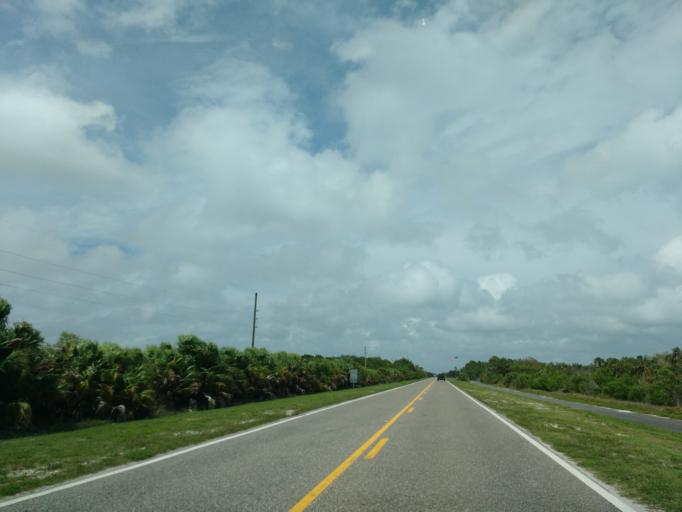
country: US
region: Florida
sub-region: Pinellas County
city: Tierra Verde
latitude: 27.6184
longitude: -82.7260
